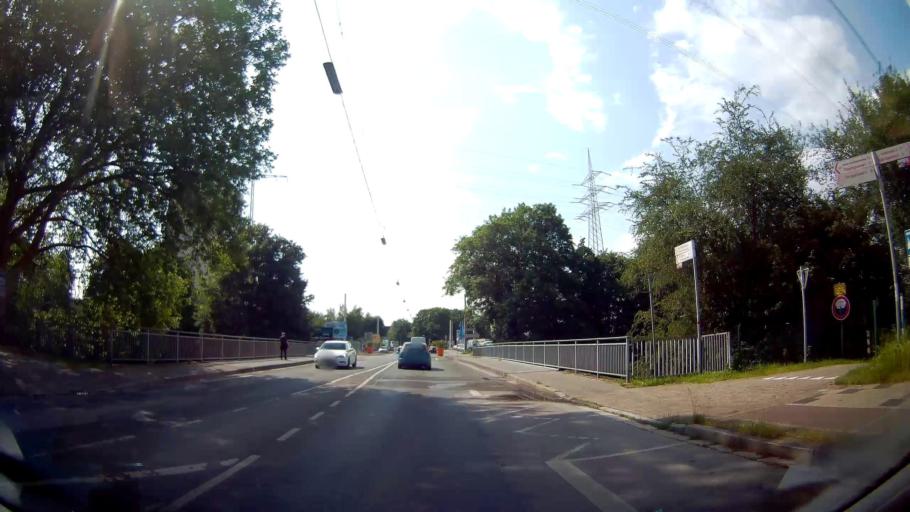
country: DE
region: North Rhine-Westphalia
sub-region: Regierungsbezirk Arnsberg
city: Herne
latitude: 51.5610
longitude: 7.2076
